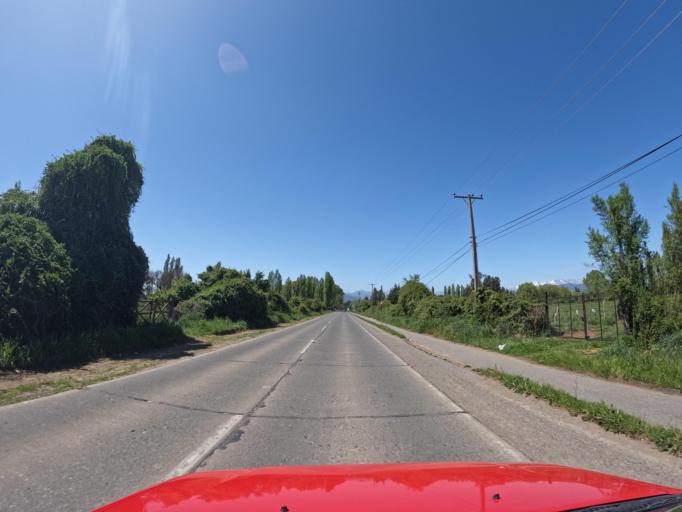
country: CL
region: Maule
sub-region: Provincia de Linares
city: Linares
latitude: -35.8282
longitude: -71.4964
